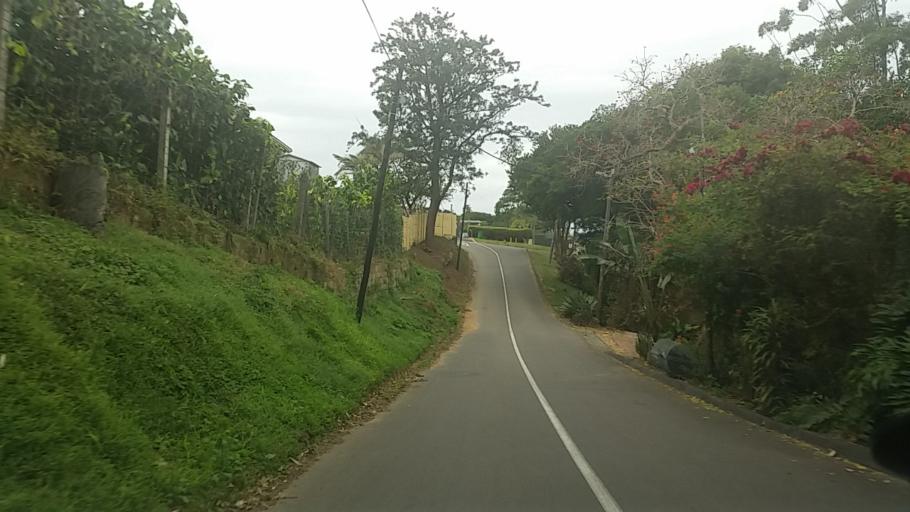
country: ZA
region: KwaZulu-Natal
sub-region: eThekwini Metropolitan Municipality
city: Berea
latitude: -29.8396
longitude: 30.9370
